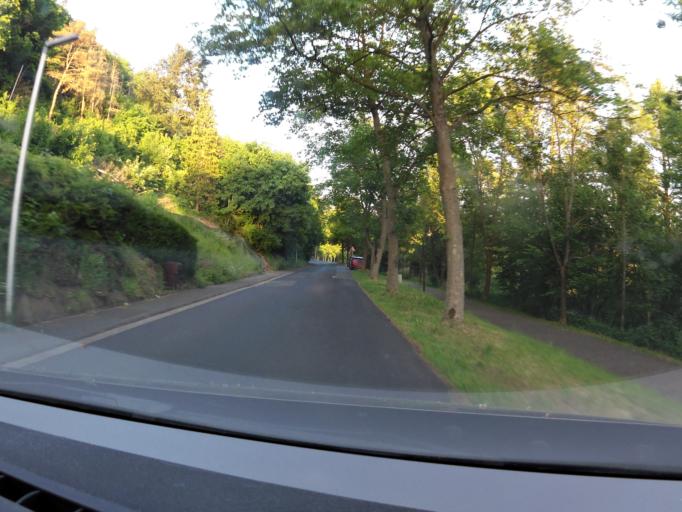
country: DE
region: Thuringia
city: Vacha
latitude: 50.8342
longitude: 10.0170
